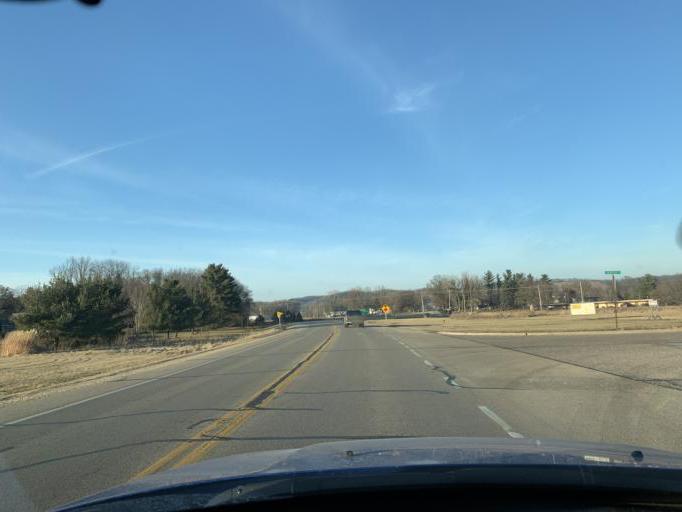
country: US
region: Wisconsin
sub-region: Sauk County
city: Spring Green
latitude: 43.1833
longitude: -90.0640
